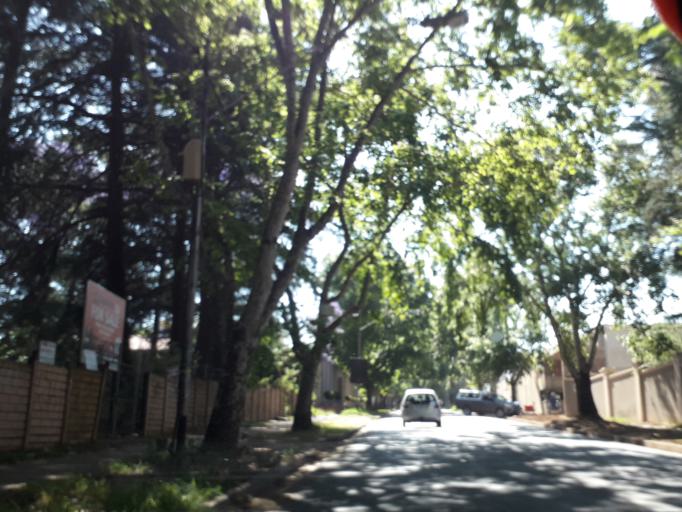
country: ZA
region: Gauteng
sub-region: City of Johannesburg Metropolitan Municipality
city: Johannesburg
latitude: -26.1557
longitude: 28.0599
